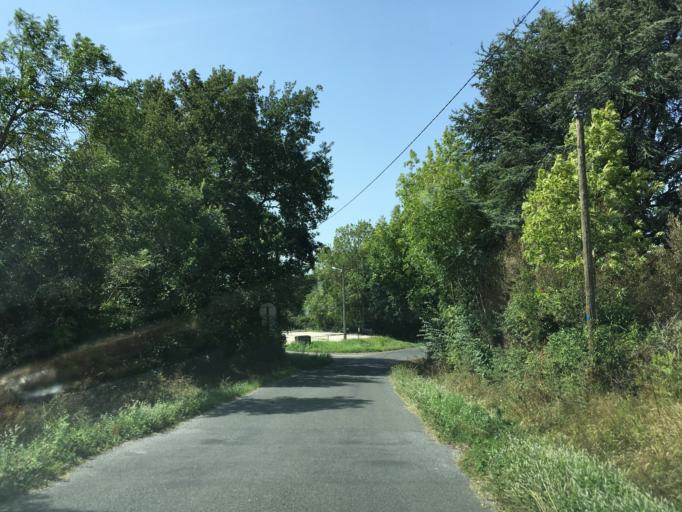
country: FR
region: Midi-Pyrenees
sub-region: Departement du Tarn
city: Lagarrigue
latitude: 43.6148
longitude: 2.2864
